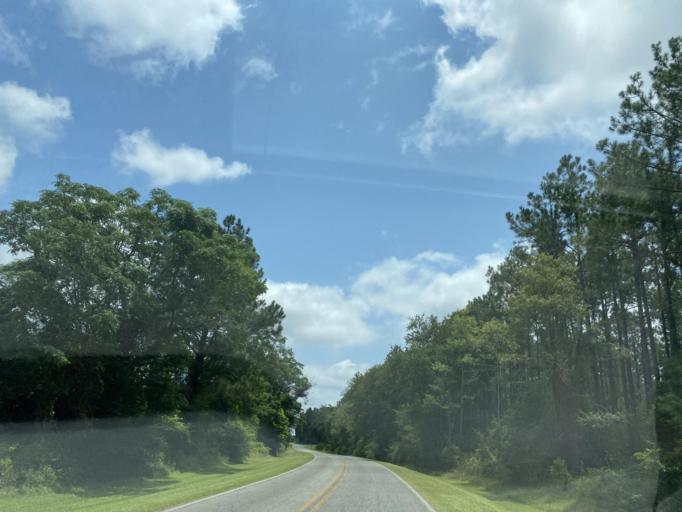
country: US
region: Georgia
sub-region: Wheeler County
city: Alamo
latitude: 32.1033
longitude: -82.7702
